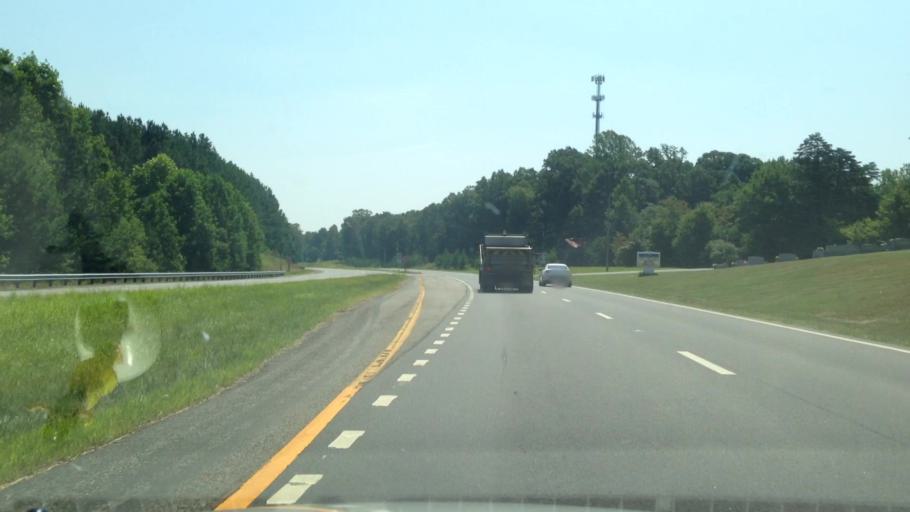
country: US
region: Virginia
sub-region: Patrick County
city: Patrick Springs
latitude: 36.5871
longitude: -80.1399
